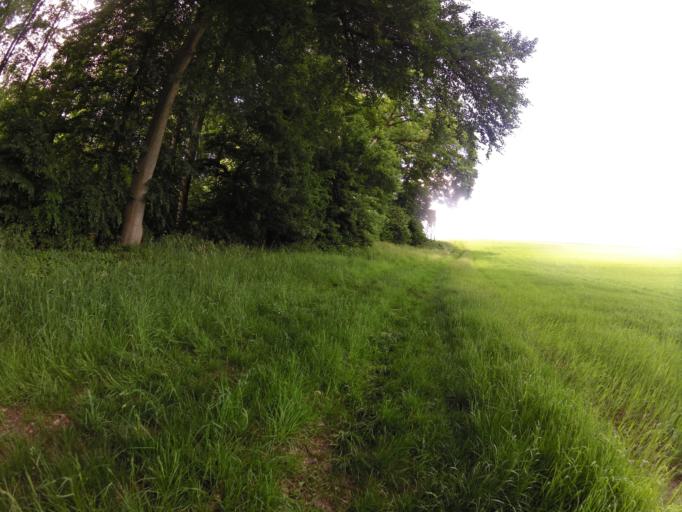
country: DE
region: Bavaria
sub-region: Regierungsbezirk Unterfranken
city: Uettingen
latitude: 49.7744
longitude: 9.7645
